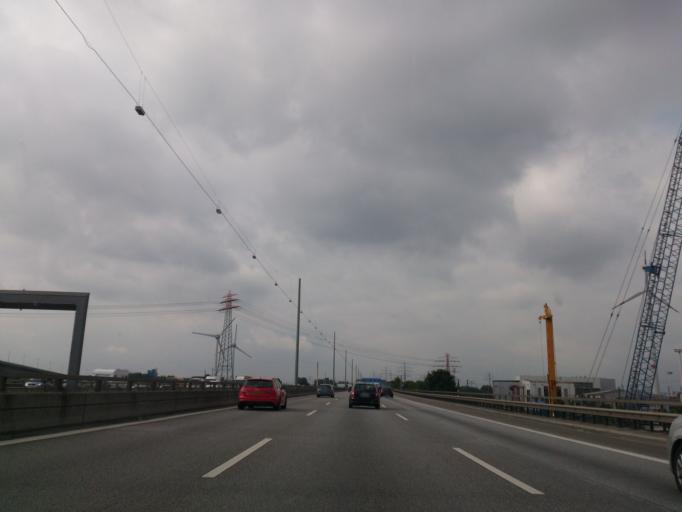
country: DE
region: Hamburg
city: Altona
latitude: 53.5249
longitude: 9.9297
